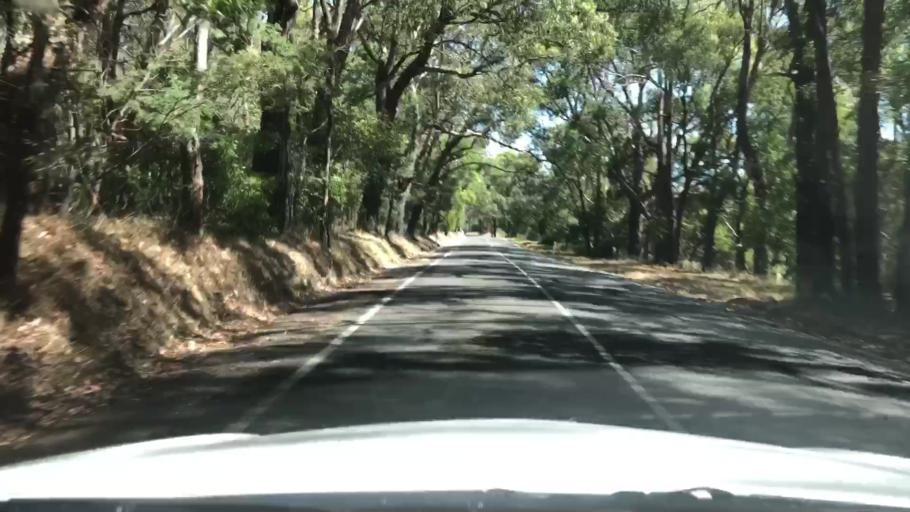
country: AU
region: Victoria
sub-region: Yarra Ranges
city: Macclesfield
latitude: -37.8302
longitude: 145.4883
